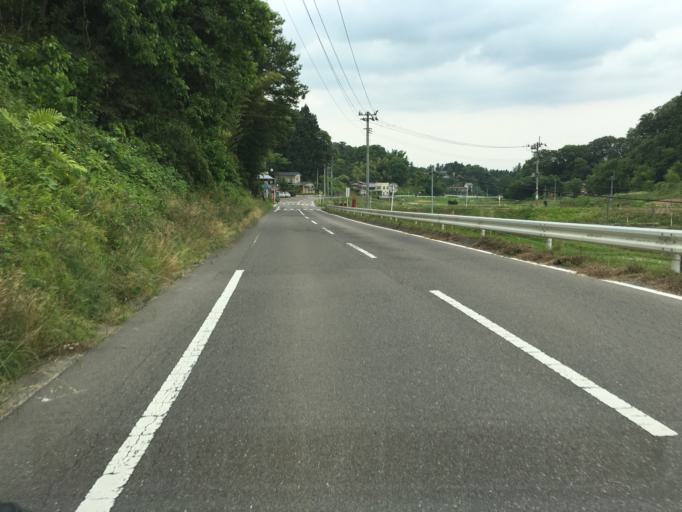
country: JP
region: Fukushima
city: Nihommatsu
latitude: 37.6371
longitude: 140.5375
